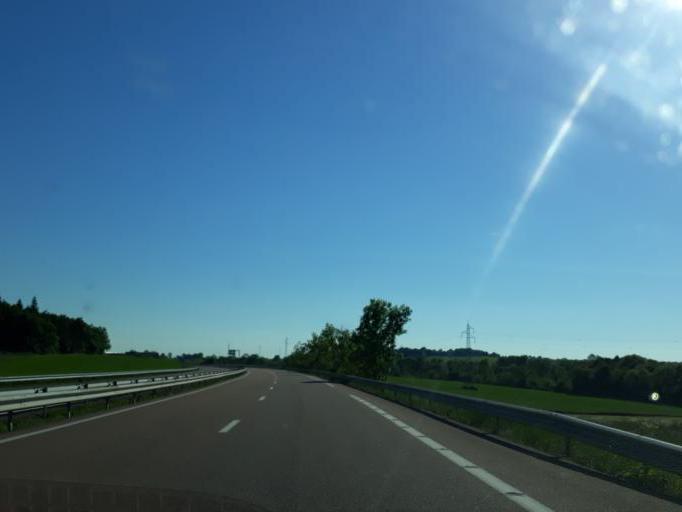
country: FR
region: Bourgogne
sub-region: Departement de la Cote-d'Or
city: Pouilly-en-Auxois
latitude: 47.2895
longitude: 4.6317
